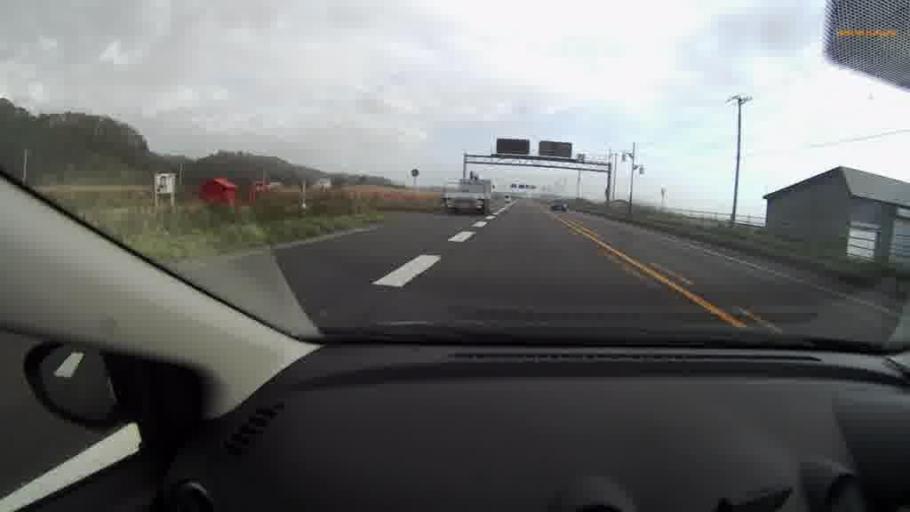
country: JP
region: Hokkaido
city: Kushiro
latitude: 42.9645
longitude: 144.1149
